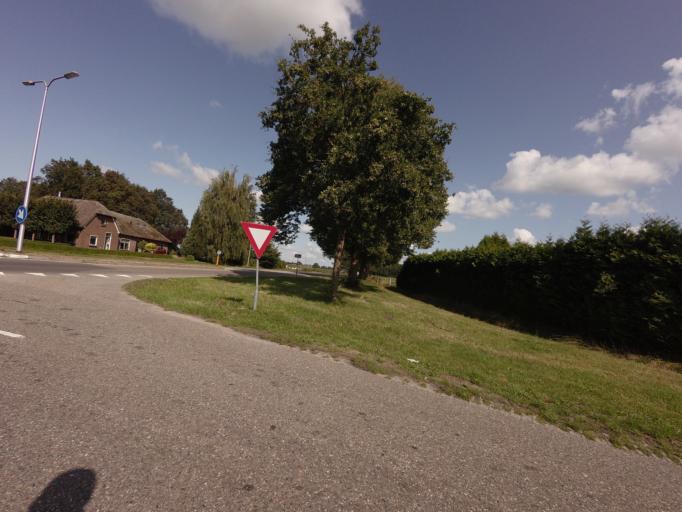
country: NL
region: Overijssel
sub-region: Gemeente Dalfsen
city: Dalfsen
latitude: 52.5287
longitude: 6.2614
